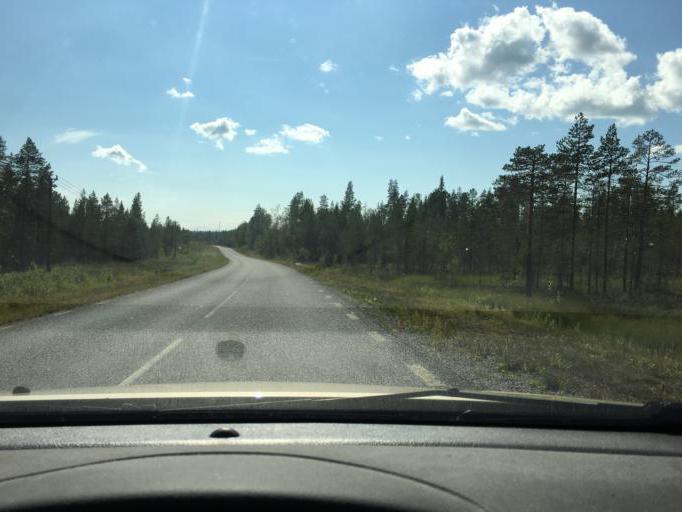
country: SE
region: Norrbotten
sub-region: Kalix Kommun
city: Toere
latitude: 66.0608
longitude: 22.6038
